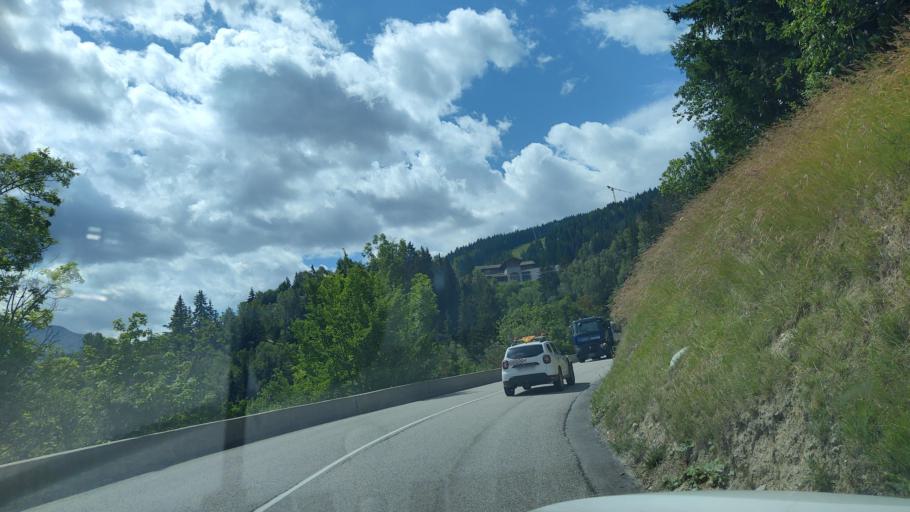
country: FR
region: Rhone-Alpes
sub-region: Departement de la Savoie
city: Saint-Bon-Tarentaise
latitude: 45.4271
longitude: 6.6399
